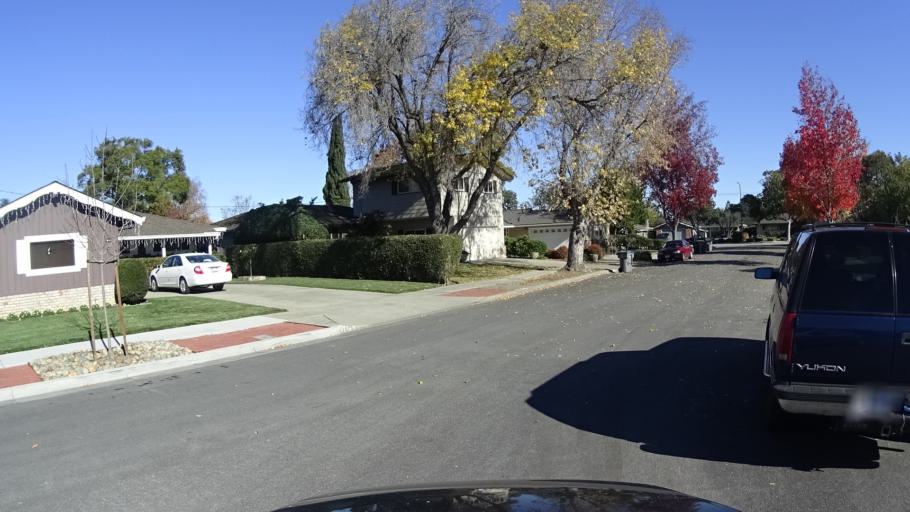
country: US
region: California
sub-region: Santa Clara County
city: Cupertino
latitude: 37.3432
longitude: -122.0043
